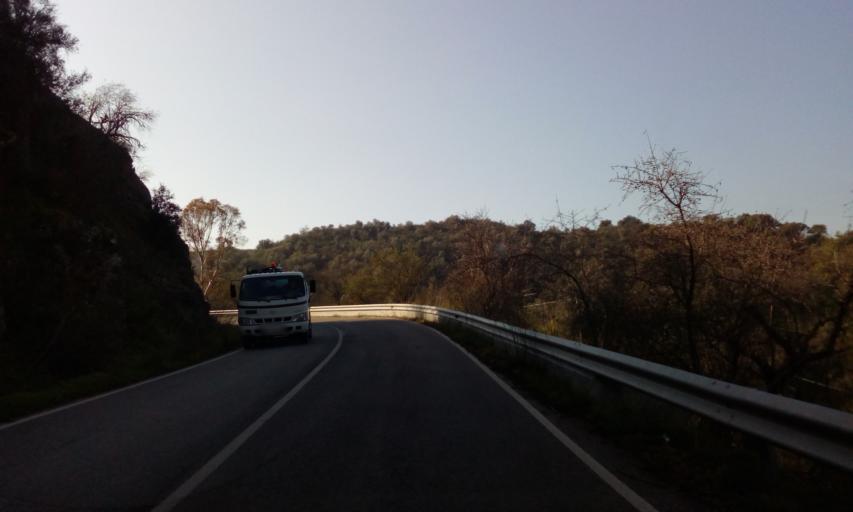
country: PT
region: Faro
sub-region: Alcoutim
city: Alcoutim
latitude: 37.4686
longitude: -7.4776
